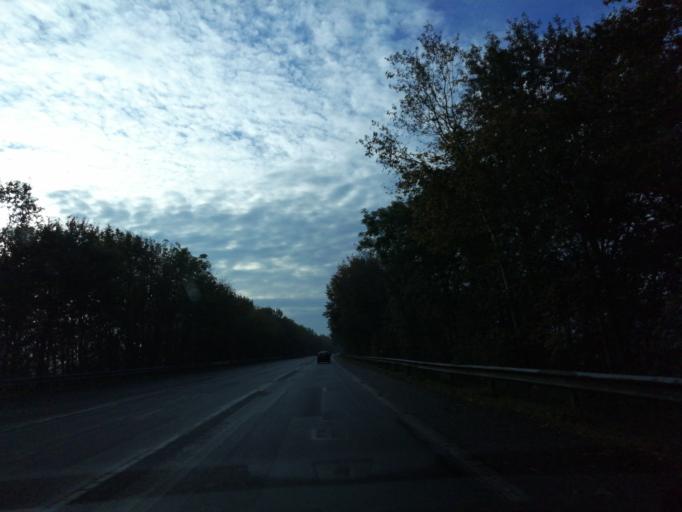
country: DE
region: Lower Saxony
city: Fedderwarden
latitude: 53.5919
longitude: 8.0544
